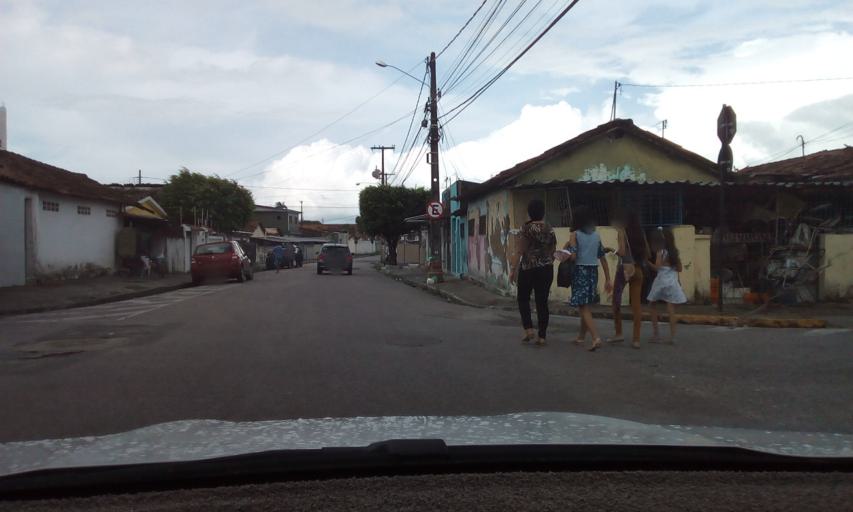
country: BR
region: Paraiba
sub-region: Joao Pessoa
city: Joao Pessoa
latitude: -7.1398
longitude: -34.8876
